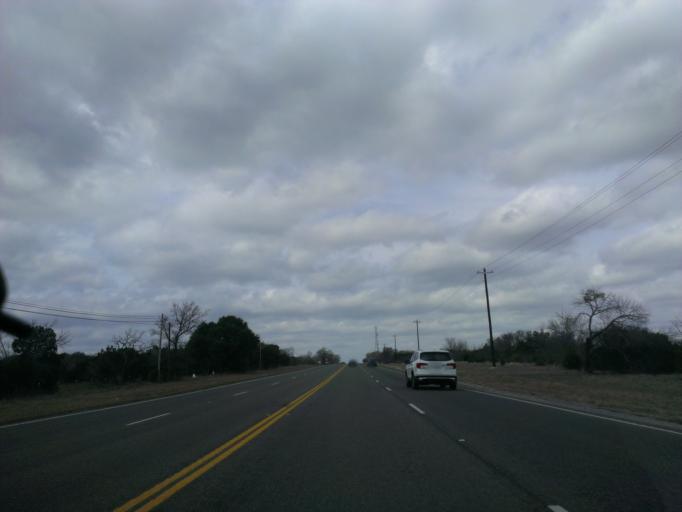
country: US
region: Texas
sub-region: Burnet County
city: Marble Falls
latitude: 30.4759
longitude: -98.1872
